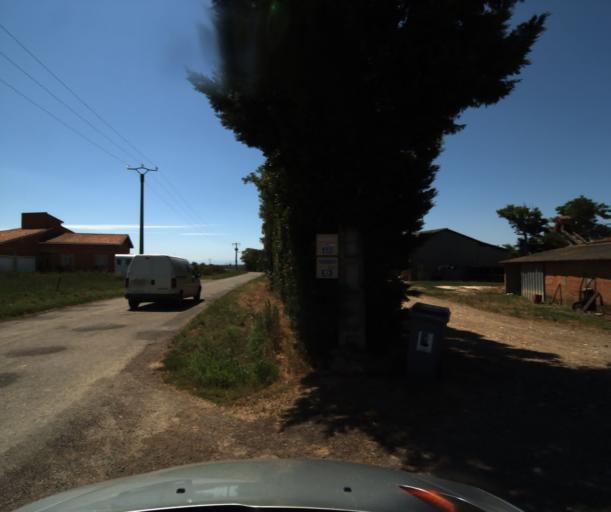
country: FR
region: Midi-Pyrenees
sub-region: Departement de la Haute-Garonne
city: Roquettes
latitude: 43.4878
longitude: 1.3684
